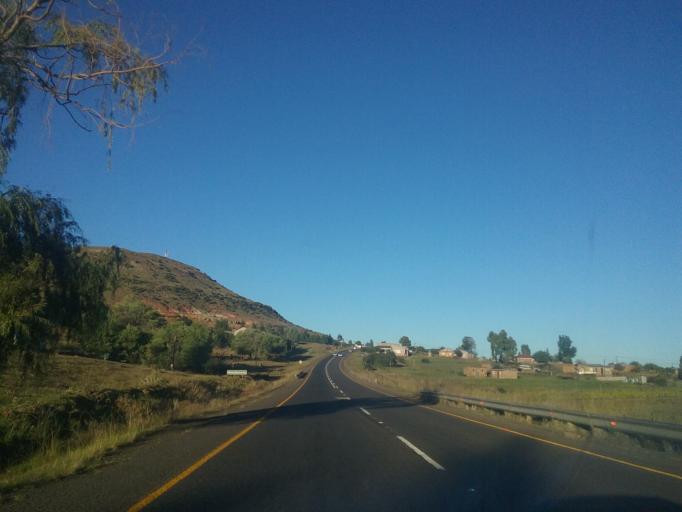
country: LS
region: Mohale's Hoek District
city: Mohale's Hoek
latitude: -30.1840
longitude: 27.4242
